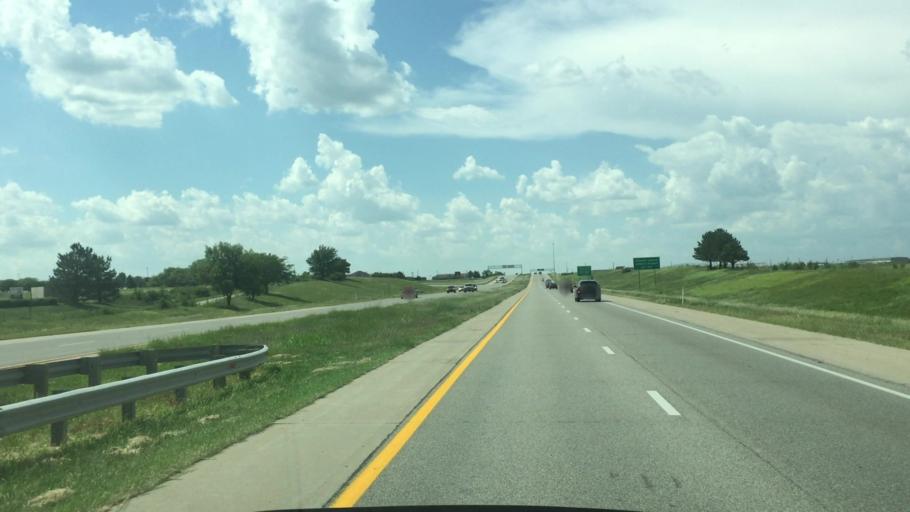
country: US
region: Kansas
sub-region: Sedgwick County
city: Bellaire
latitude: 37.7324
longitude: -97.2195
